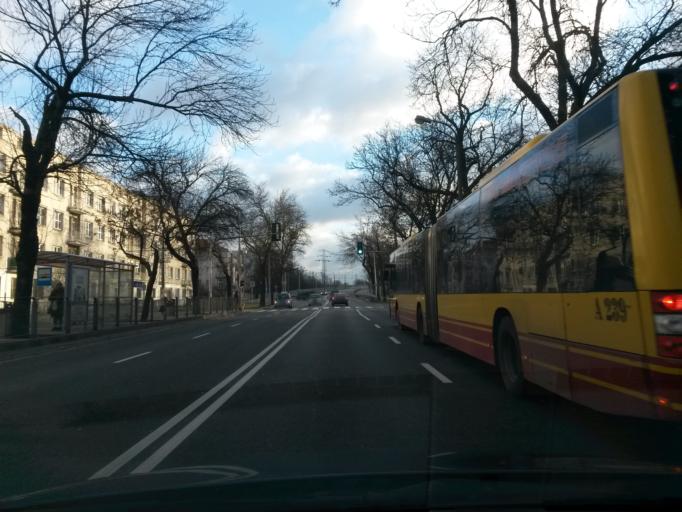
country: PL
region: Masovian Voivodeship
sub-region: Warszawa
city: Zoliborz
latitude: 52.2623
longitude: 20.9924
